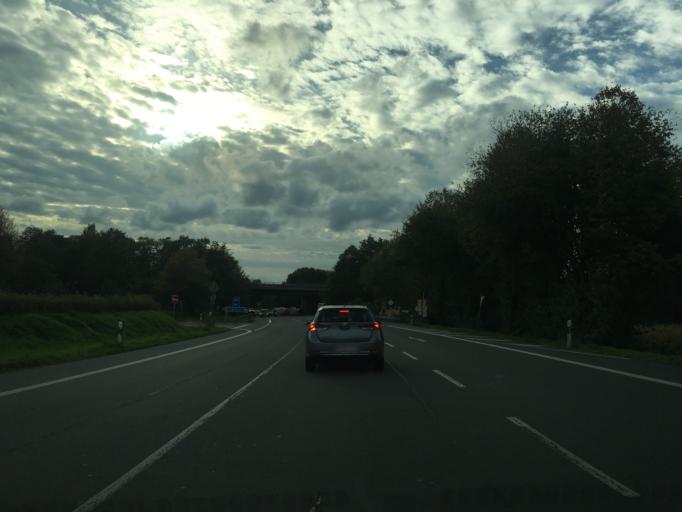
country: DE
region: North Rhine-Westphalia
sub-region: Regierungsbezirk Munster
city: Haltern
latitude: 51.7833
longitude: 7.1800
